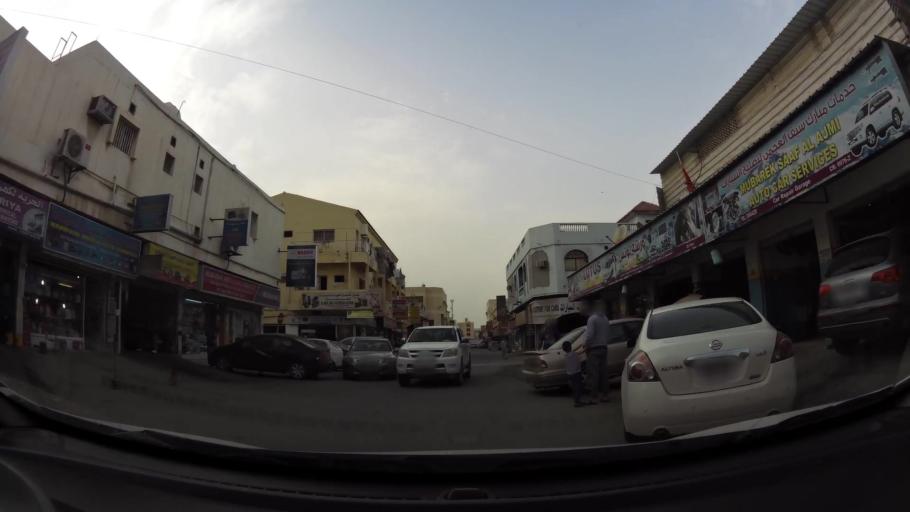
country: BH
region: Northern
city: Ar Rifa'
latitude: 26.1224
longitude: 50.5673
